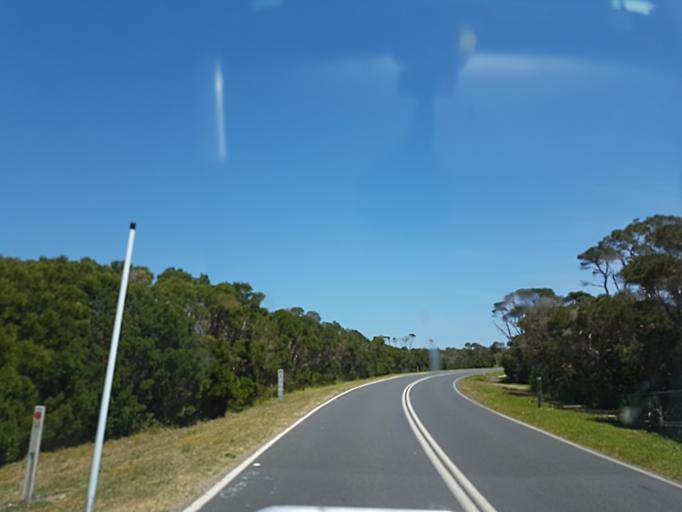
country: AU
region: Victoria
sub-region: Bass Coast
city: North Wonthaggi
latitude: -38.7001
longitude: 145.8772
